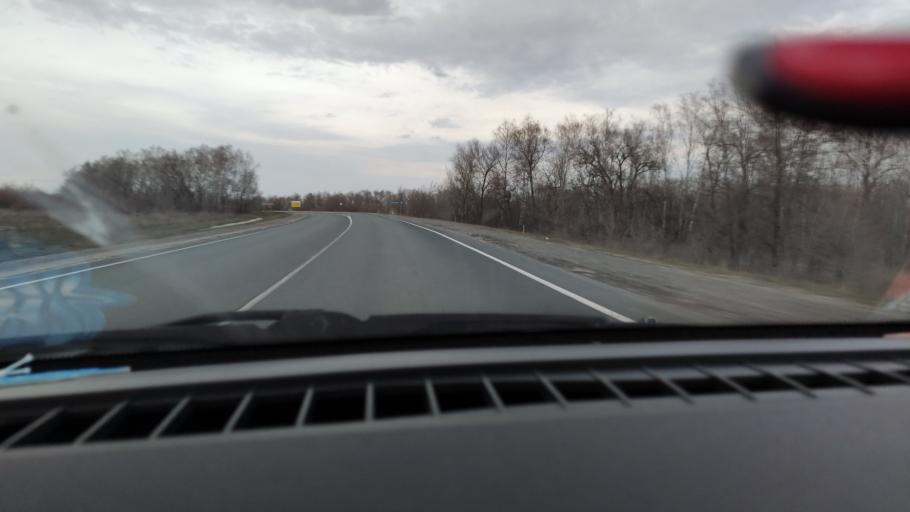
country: RU
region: Saratov
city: Sinodskoye
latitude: 51.9380
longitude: 46.5935
